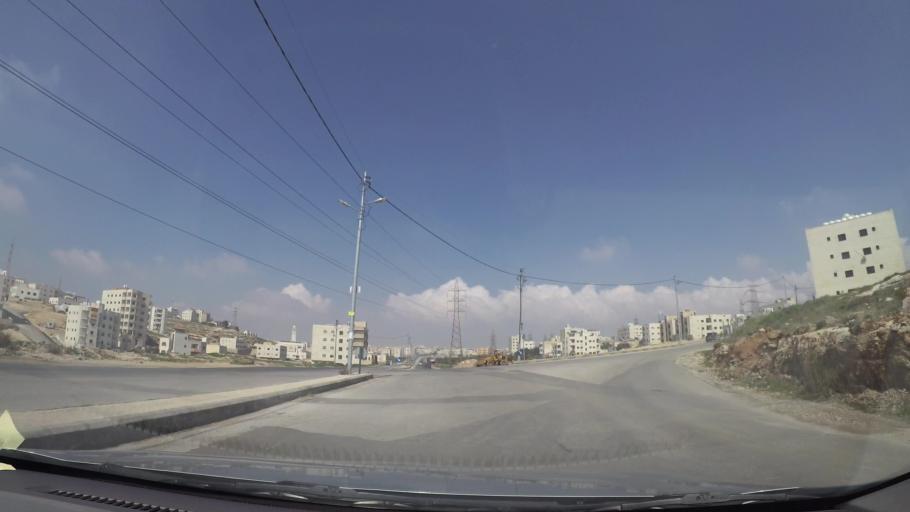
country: JO
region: Amman
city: Al Bunayyat ash Shamaliyah
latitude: 31.8884
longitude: 35.9024
